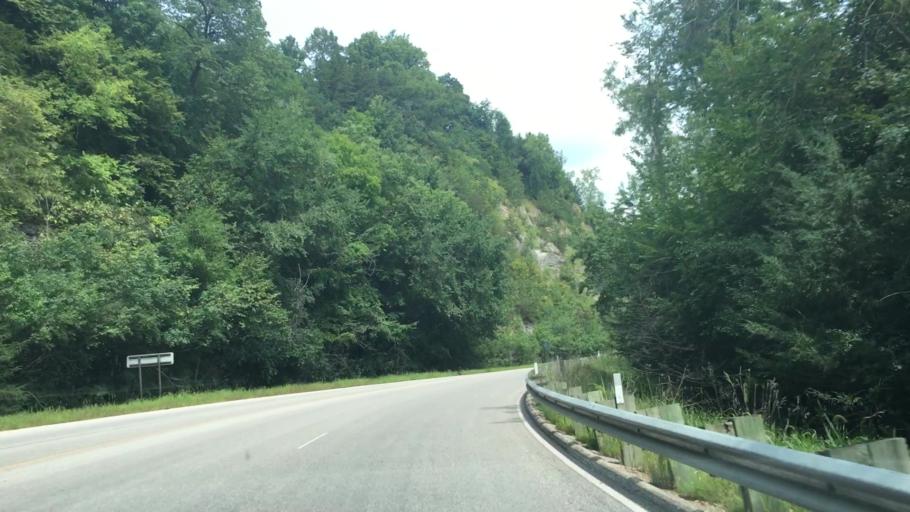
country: US
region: Minnesota
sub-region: Fillmore County
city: Preston
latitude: 43.7223
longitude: -91.9812
